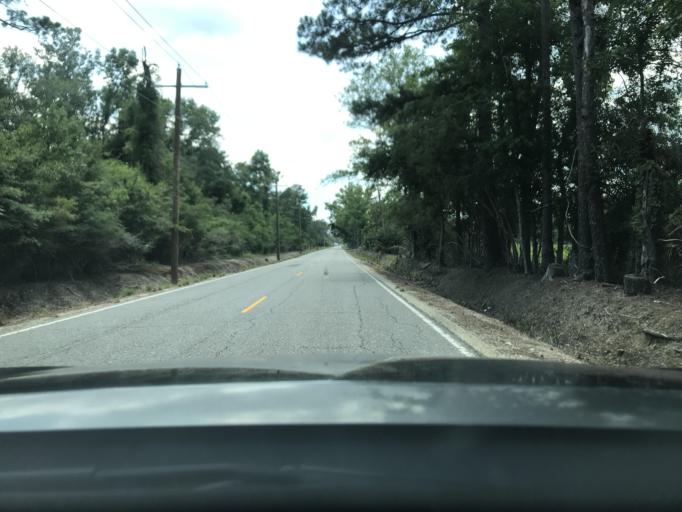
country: US
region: Louisiana
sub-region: Calcasieu Parish
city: Moss Bluff
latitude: 30.3300
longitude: -93.1602
